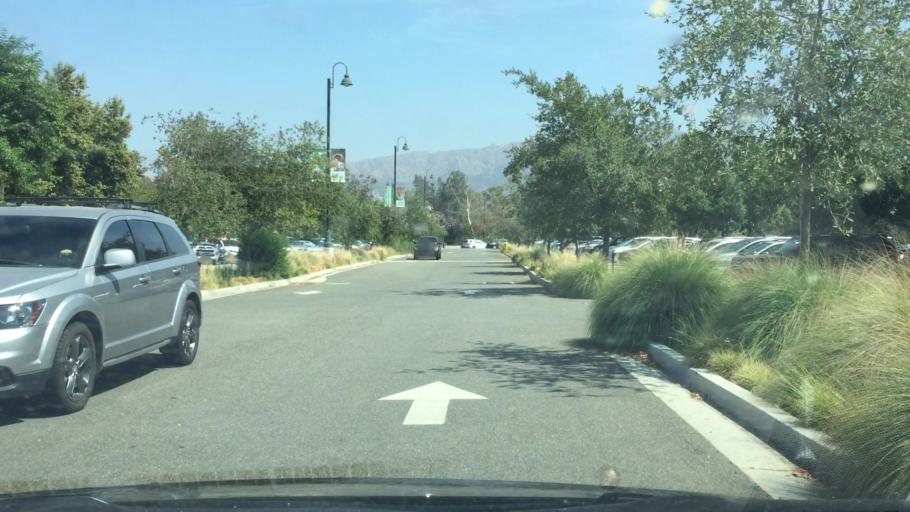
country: US
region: California
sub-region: Los Angeles County
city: North Glendale
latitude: 34.1485
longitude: -118.2835
